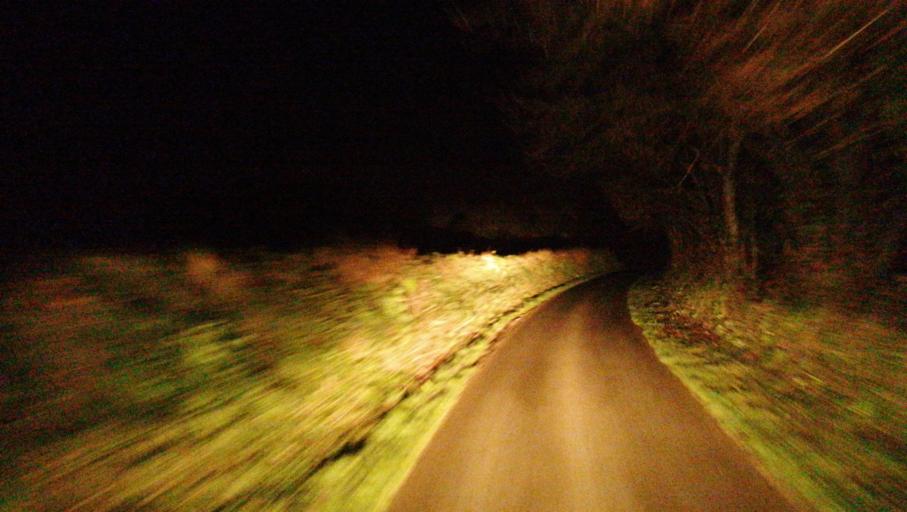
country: FR
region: Brittany
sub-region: Departement des Cotes-d'Armor
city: Plehedel
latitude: 48.6778
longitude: -3.0313
